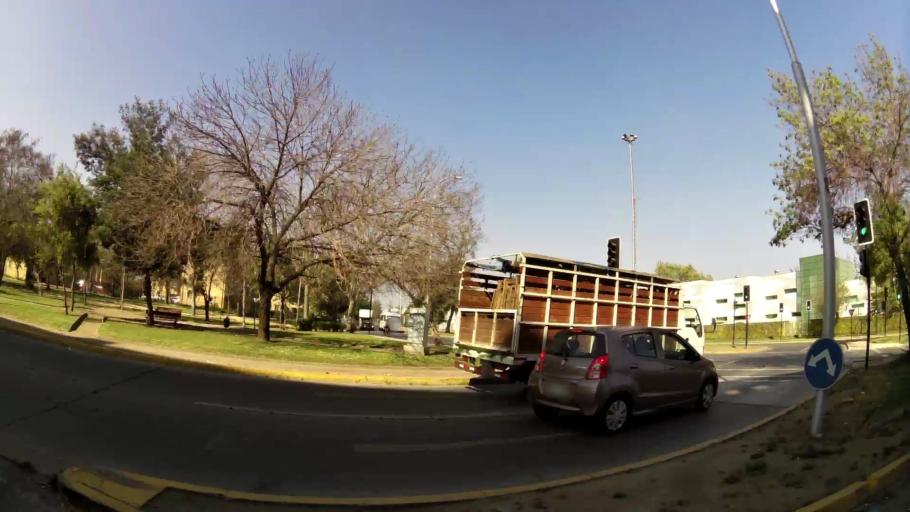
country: CL
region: Santiago Metropolitan
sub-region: Provincia de Santiago
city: Santiago
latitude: -33.4711
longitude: -70.6230
